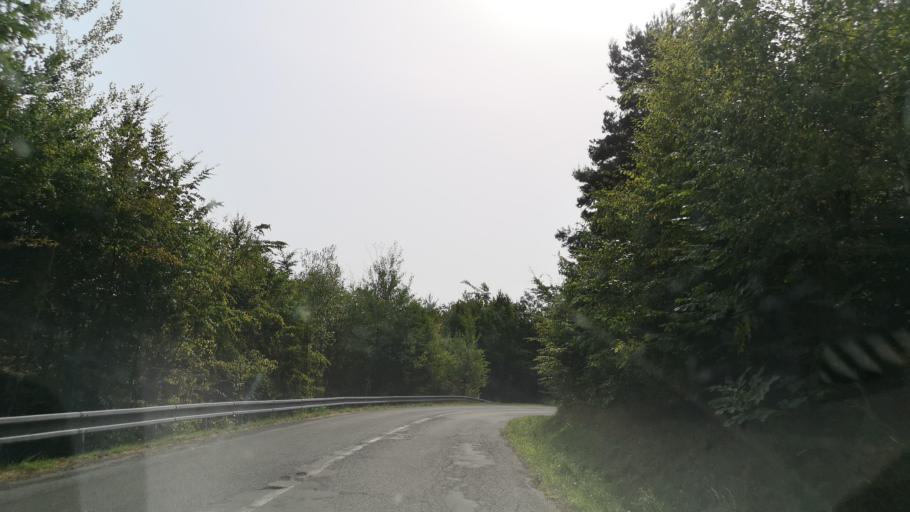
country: SK
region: Banskobystricky
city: Revuca
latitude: 48.5830
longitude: 20.0694
